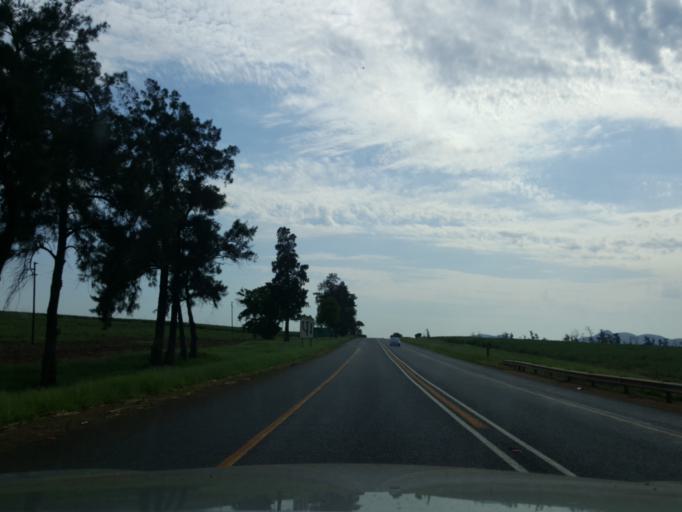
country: SZ
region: Hhohho
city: Ntfonjeni
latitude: -25.5113
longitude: 31.4684
